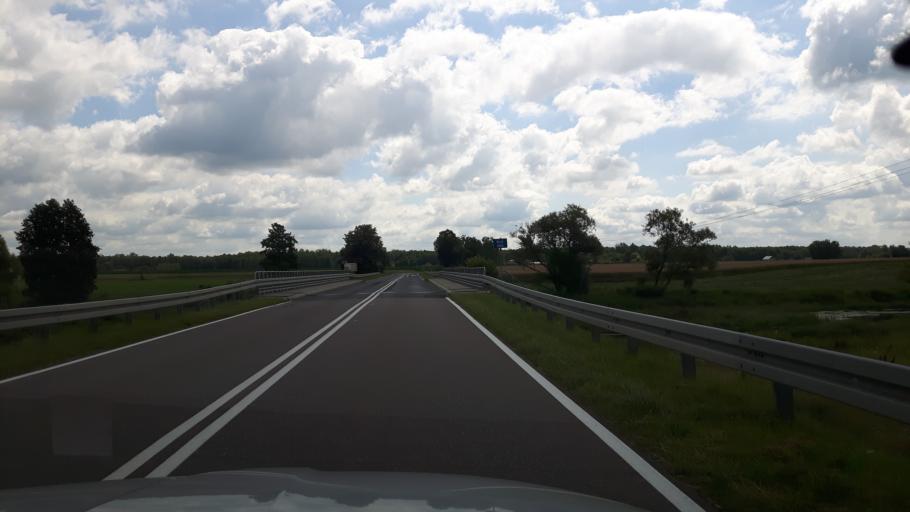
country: PL
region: Masovian Voivodeship
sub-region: Powiat ostrowski
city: Brok
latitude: 52.7032
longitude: 21.9051
